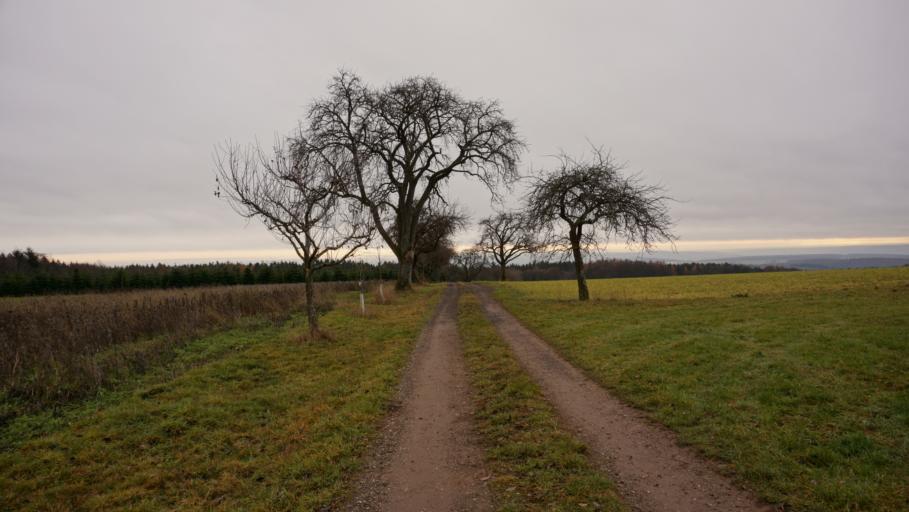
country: DE
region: Baden-Wuerttemberg
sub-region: Karlsruhe Region
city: Fahrenbach
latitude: 49.4456
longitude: 9.1128
